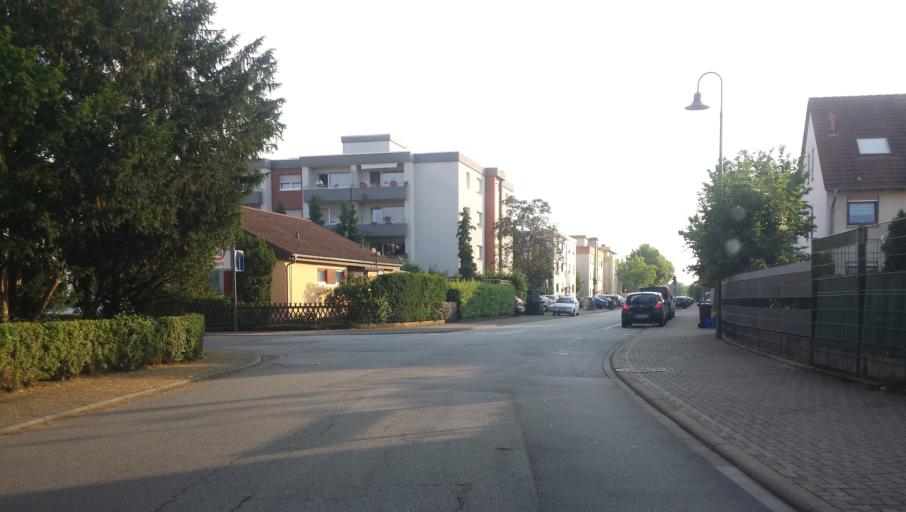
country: DE
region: Baden-Wuerttemberg
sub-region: Karlsruhe Region
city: Bruhl
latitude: 49.4085
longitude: 8.5312
